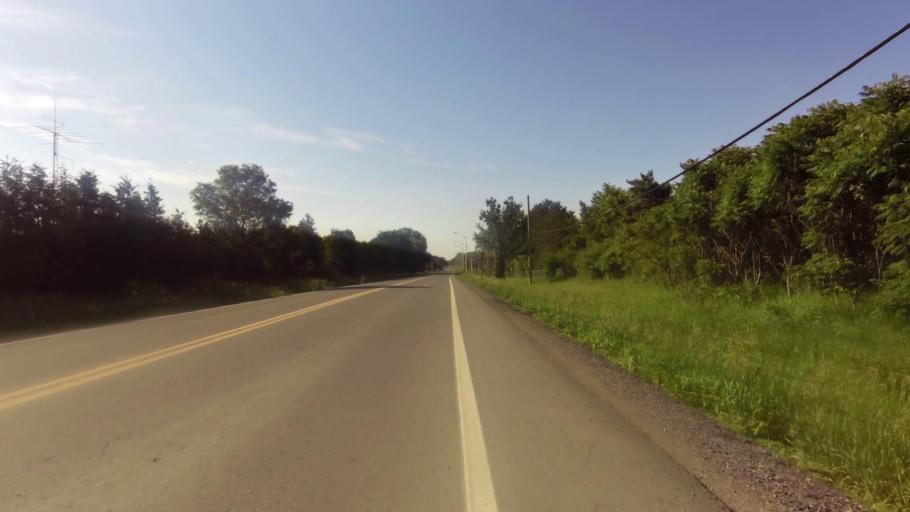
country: CA
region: Ontario
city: Ottawa
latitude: 45.2614
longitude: -75.5700
